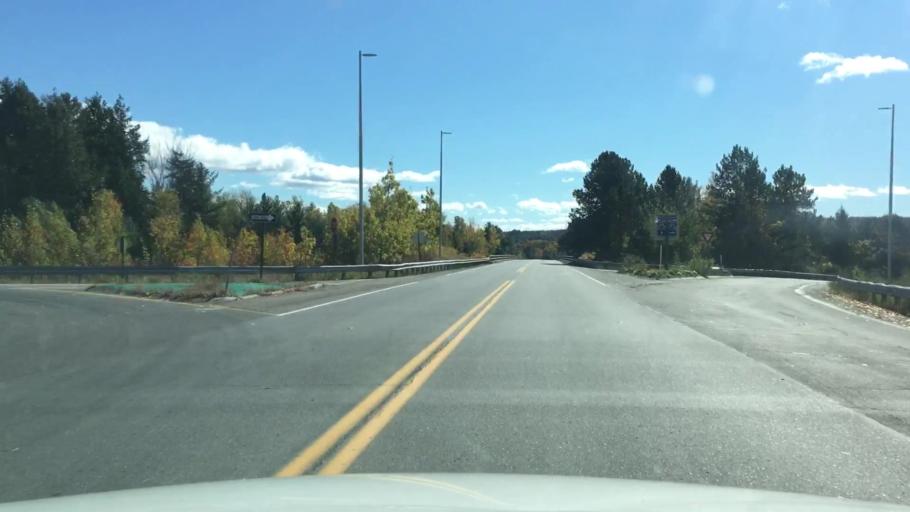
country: US
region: Maine
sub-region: Penobscot County
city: Medway
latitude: 45.6083
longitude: -68.5231
